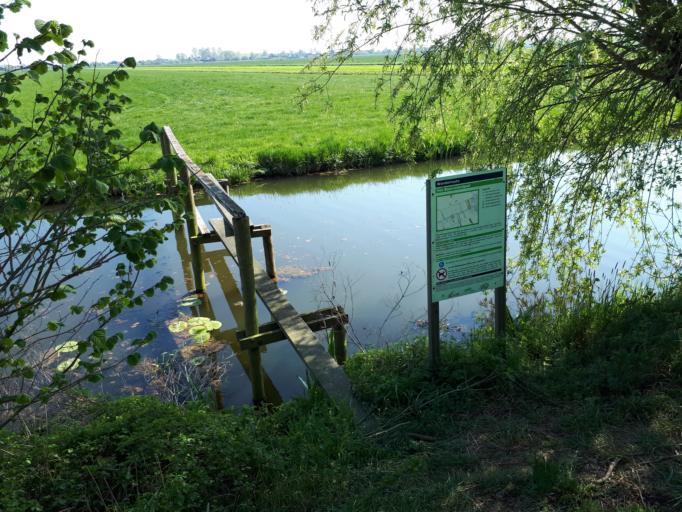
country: NL
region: Utrecht
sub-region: Gemeente IJsselstein
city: IJsselstein
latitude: 52.0219
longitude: 4.9967
